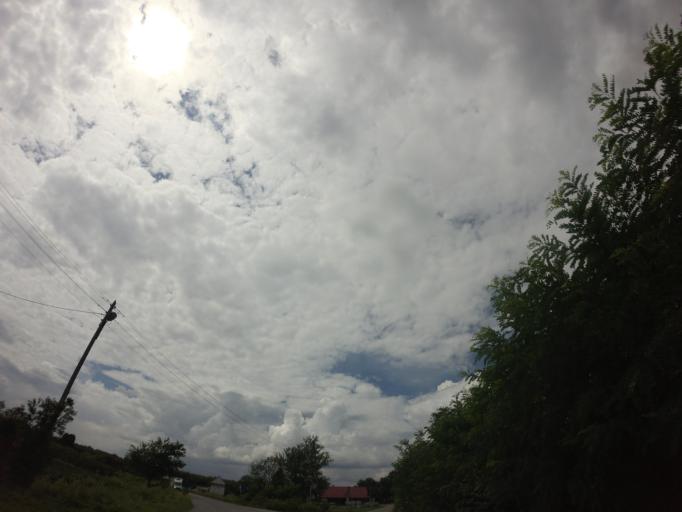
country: PL
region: Lublin Voivodeship
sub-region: Powiat pulawski
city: Kazimierz Dolny
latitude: 51.2849
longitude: 21.9368
